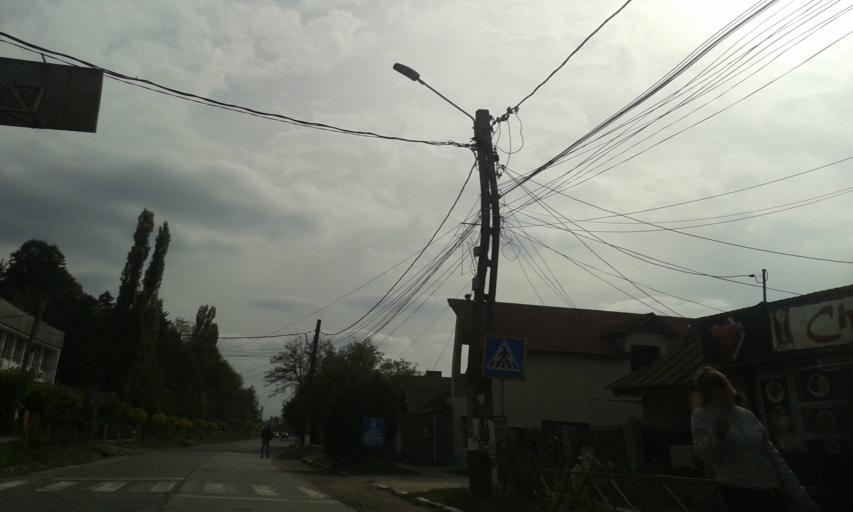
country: RO
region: Gorj
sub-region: Comuna Targu Carbunesti
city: Targu Carbunesti
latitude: 44.9601
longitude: 23.5099
